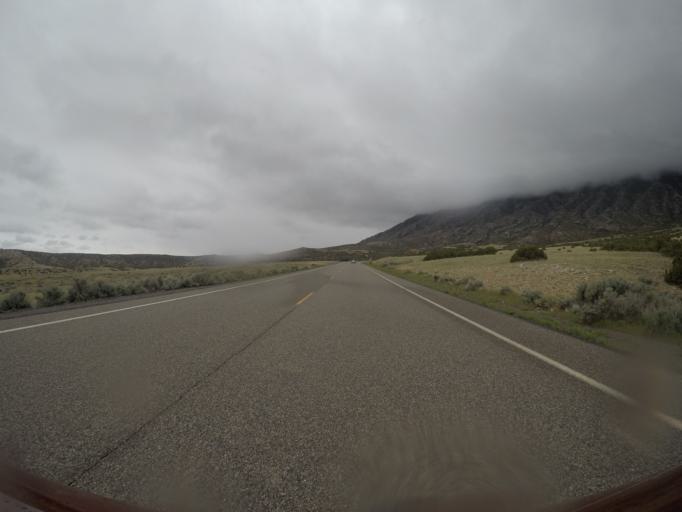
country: US
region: Wyoming
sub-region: Big Horn County
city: Lovell
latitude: 45.0644
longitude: -108.2568
